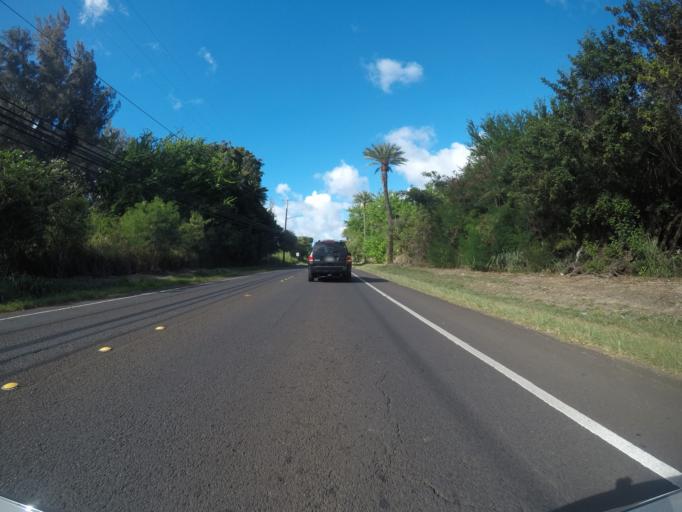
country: US
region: Hawaii
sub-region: Honolulu County
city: Hale'iwa
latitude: 21.6099
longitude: -158.0941
